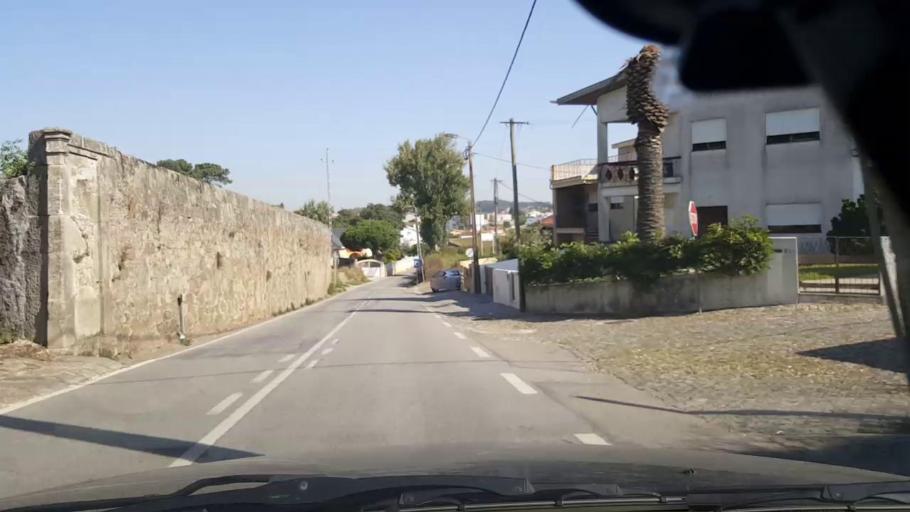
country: PT
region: Porto
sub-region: Maia
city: Gemunde
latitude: 41.2971
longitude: -8.6804
